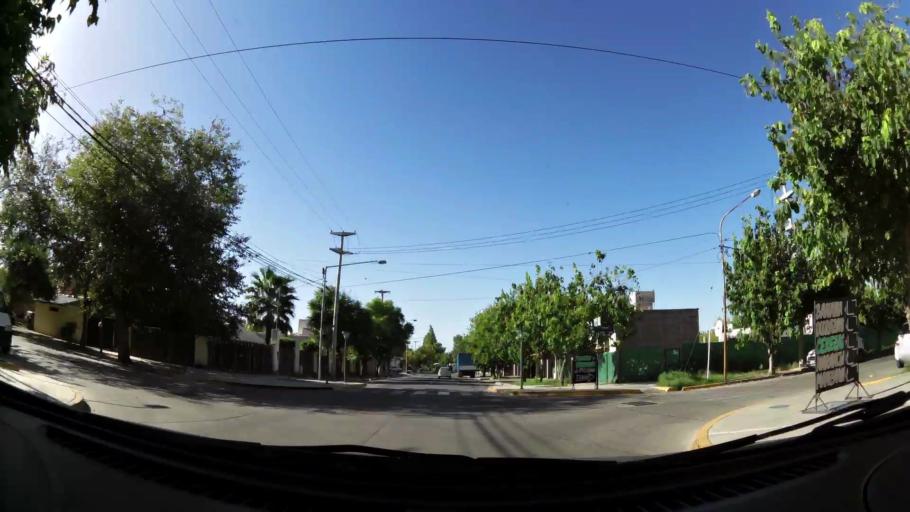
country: AR
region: Mendoza
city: Villa Nueva
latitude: -32.9112
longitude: -68.7972
